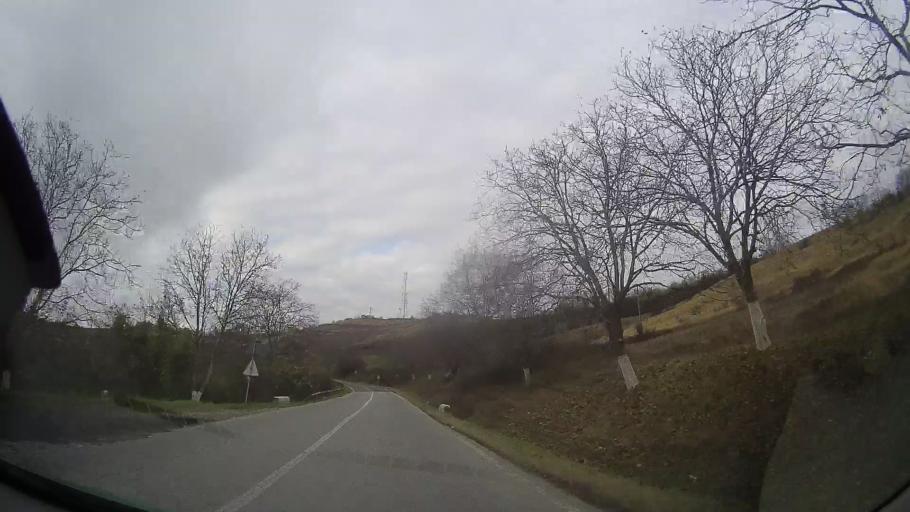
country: RO
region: Bistrita-Nasaud
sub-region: Comuna Silvasu de Campie
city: Silvasu de Campie
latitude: 46.7760
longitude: 24.3235
